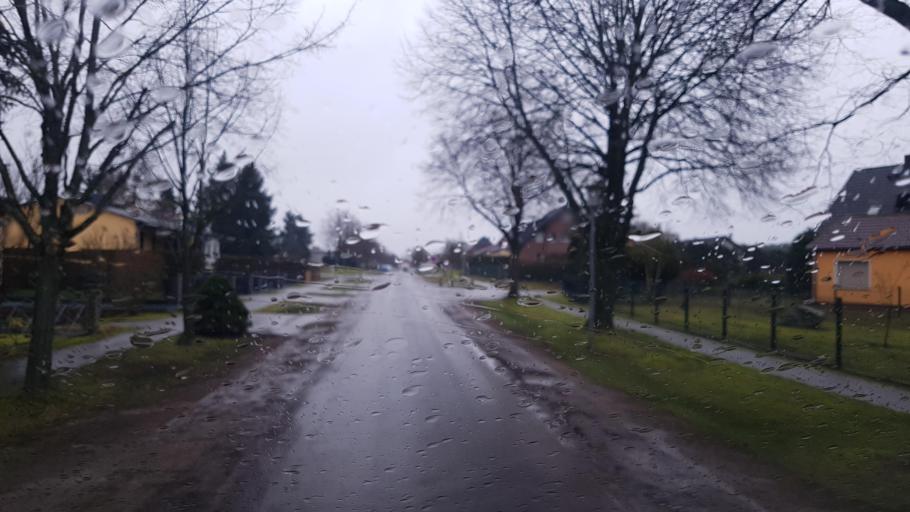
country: DE
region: Brandenburg
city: Oranienburg
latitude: 52.8446
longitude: 13.1697
